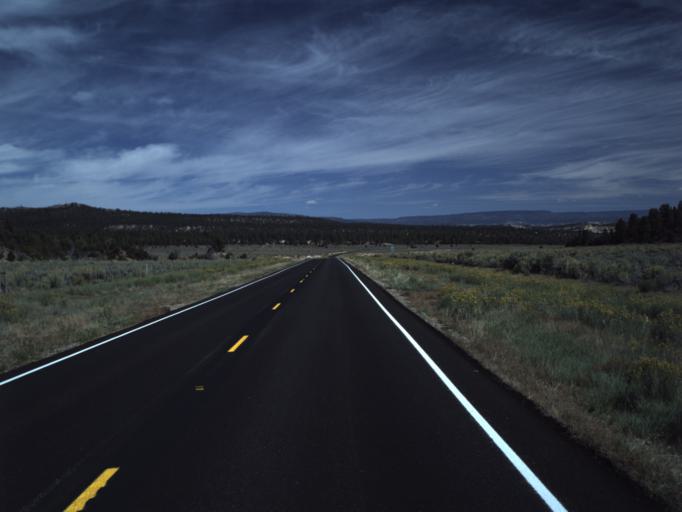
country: US
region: Utah
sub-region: Garfield County
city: Panguitch
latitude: 37.6632
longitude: -111.8326
